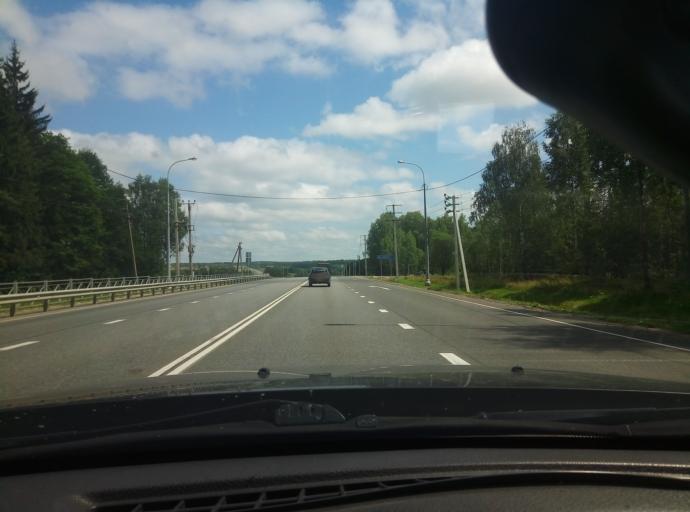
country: RU
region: Kaluga
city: Kaluga
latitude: 54.4331
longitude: 36.4248
